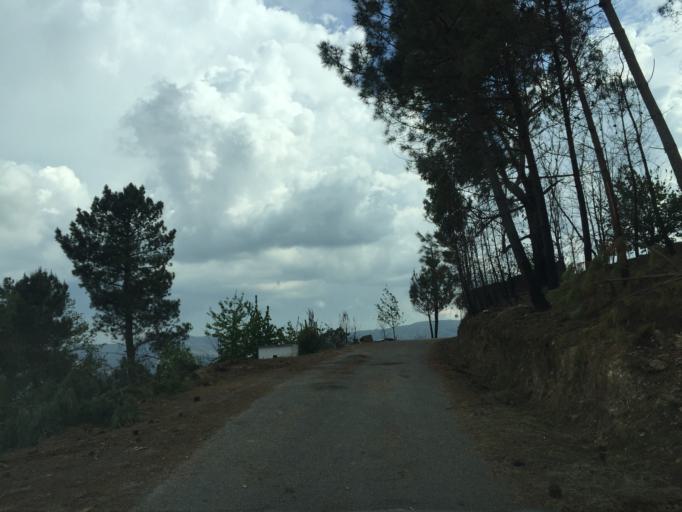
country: PT
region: Coimbra
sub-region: Arganil
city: Arganil
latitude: 40.1620
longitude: -7.9756
